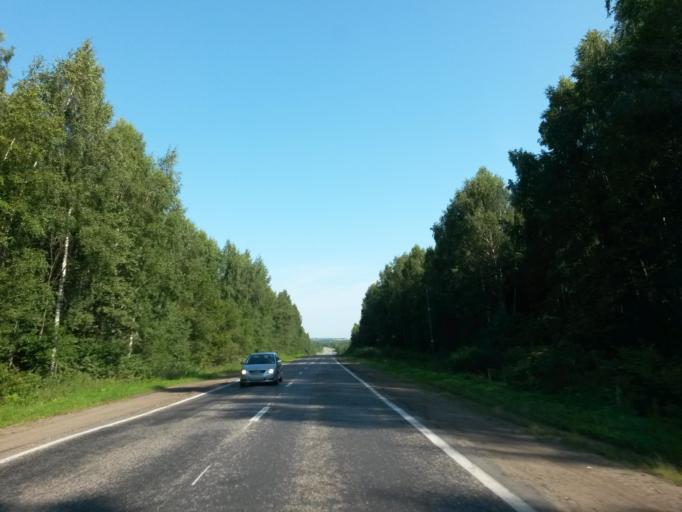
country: RU
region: Jaroslavl
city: Yaroslavl
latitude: 57.5012
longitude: 39.8994
